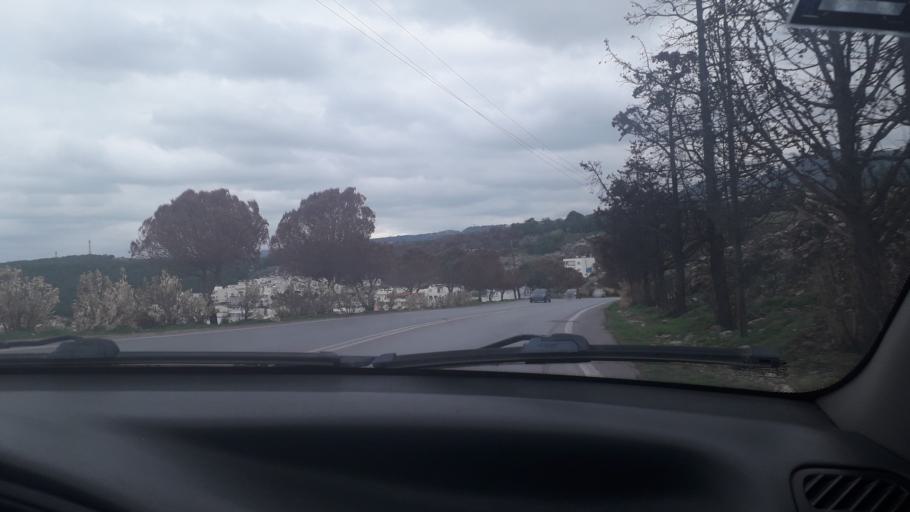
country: GR
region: Crete
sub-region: Nomos Rethymnis
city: Rethymno
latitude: 35.3589
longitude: 24.4693
